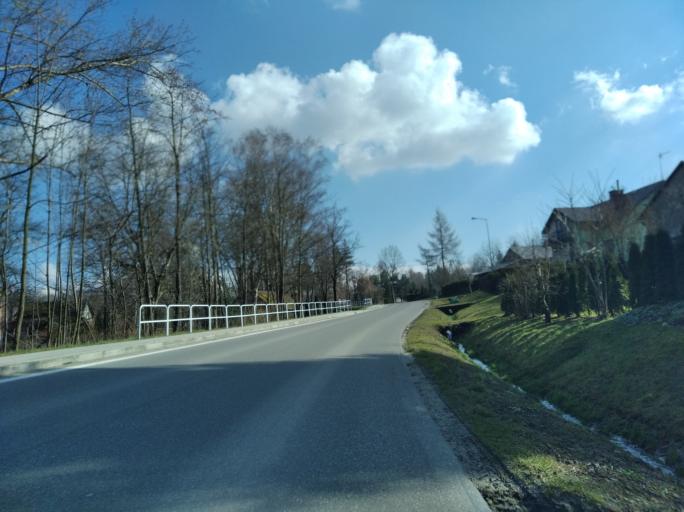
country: PL
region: Subcarpathian Voivodeship
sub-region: Powiat jasielski
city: Kolaczyce
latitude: 49.8513
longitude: 21.5157
